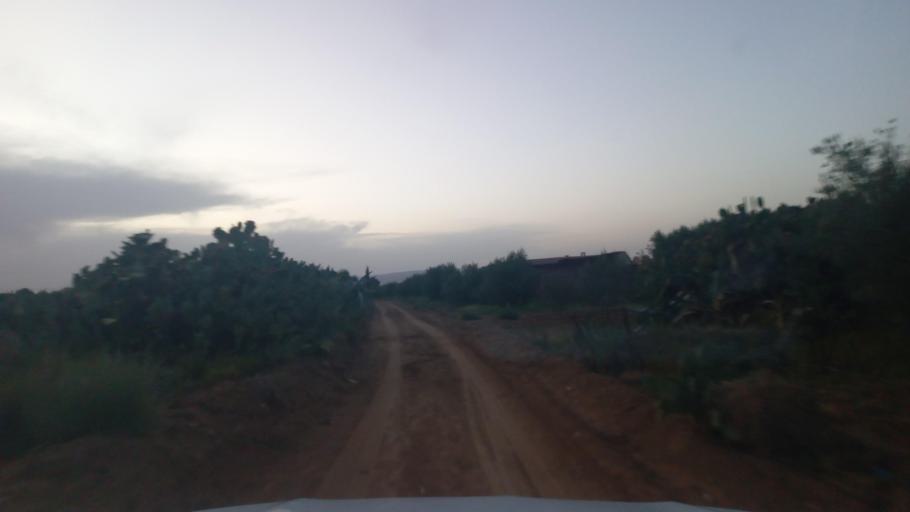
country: TN
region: Al Qasrayn
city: Kasserine
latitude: 35.2308
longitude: 9.0350
